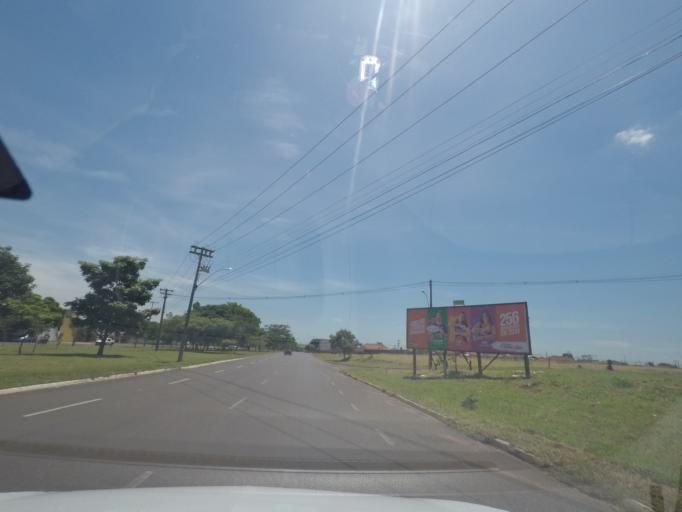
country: BR
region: Sao Paulo
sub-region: Matao
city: Matao
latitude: -21.6196
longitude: -48.3562
